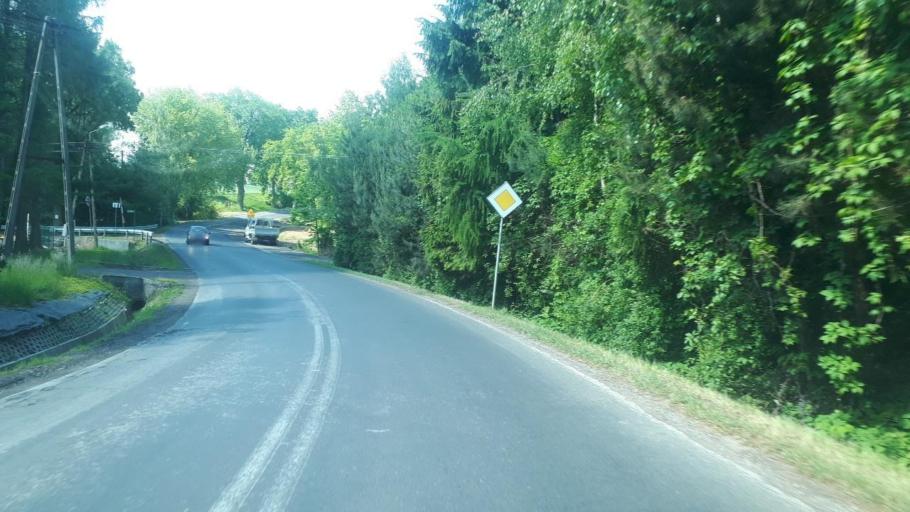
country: PL
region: Silesian Voivodeship
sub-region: Powiat bielski
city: Wilamowice
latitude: 49.9382
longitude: 19.1293
